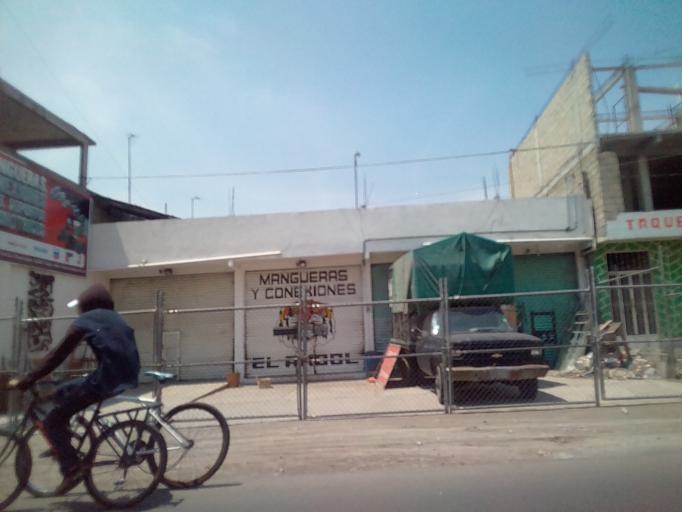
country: MX
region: Mexico
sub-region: Toluca
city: San Nicolas Tolentino
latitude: 19.3641
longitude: -99.5646
